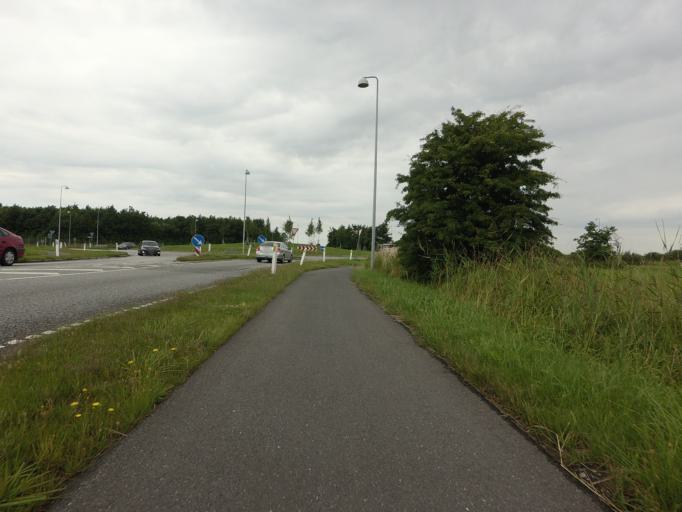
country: DK
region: North Denmark
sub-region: Alborg Kommune
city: Aalborg
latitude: 57.0837
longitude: 9.8896
